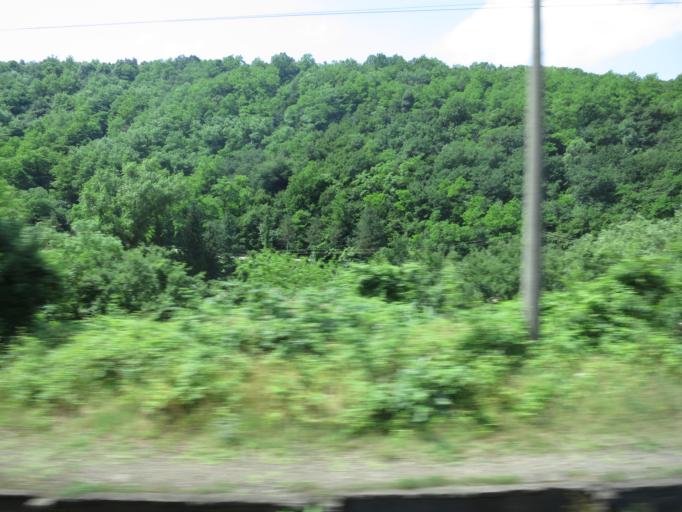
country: GE
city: Shorapani
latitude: 42.0936
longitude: 43.1300
